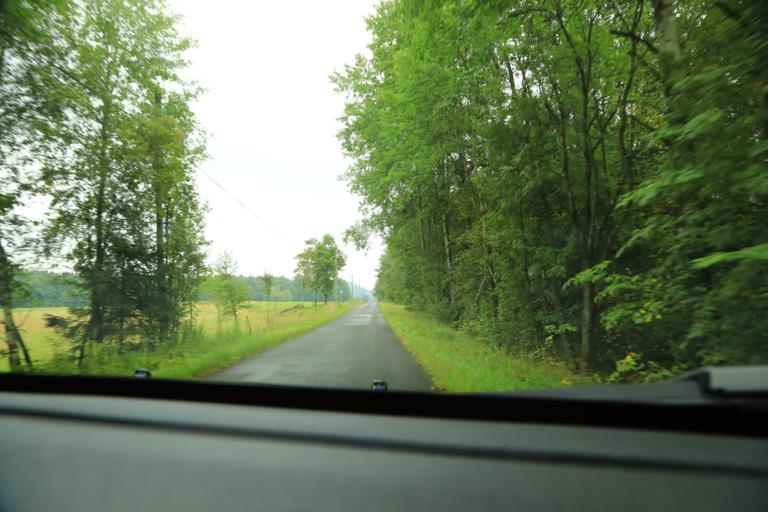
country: SE
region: Halland
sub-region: Falkenbergs Kommun
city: Falkenberg
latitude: 57.1124
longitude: 12.6804
